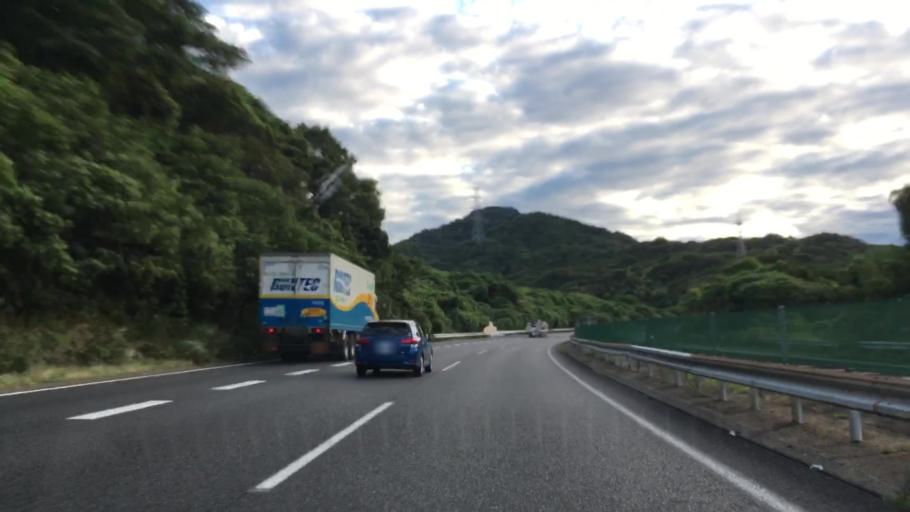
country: JP
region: Yamaguchi
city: Shimonoseki
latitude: 34.0410
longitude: 130.9845
